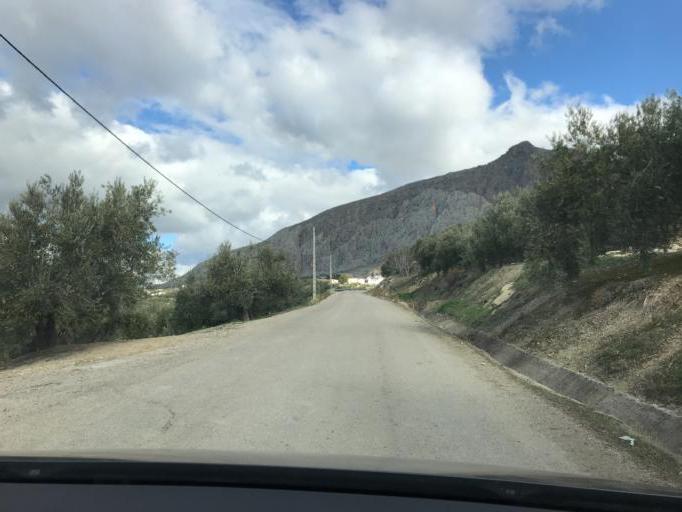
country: ES
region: Andalusia
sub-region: Provincia de Jaen
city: Jimena
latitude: 37.8171
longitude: -3.4228
